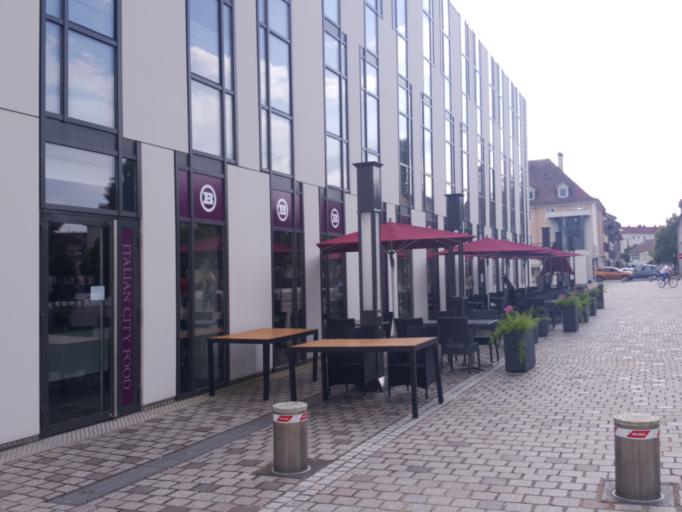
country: FR
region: Alsace
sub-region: Departement du Haut-Rhin
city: Huningue
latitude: 47.5917
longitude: 7.5850
